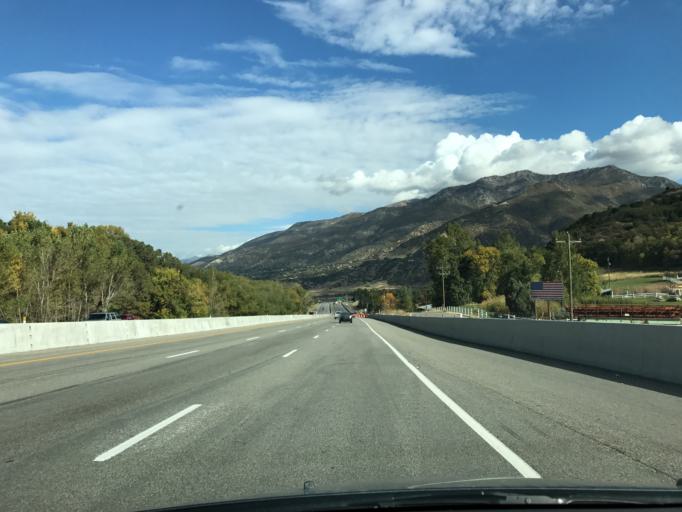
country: US
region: Utah
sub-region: Davis County
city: South Weber
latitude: 41.1111
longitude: -111.9092
